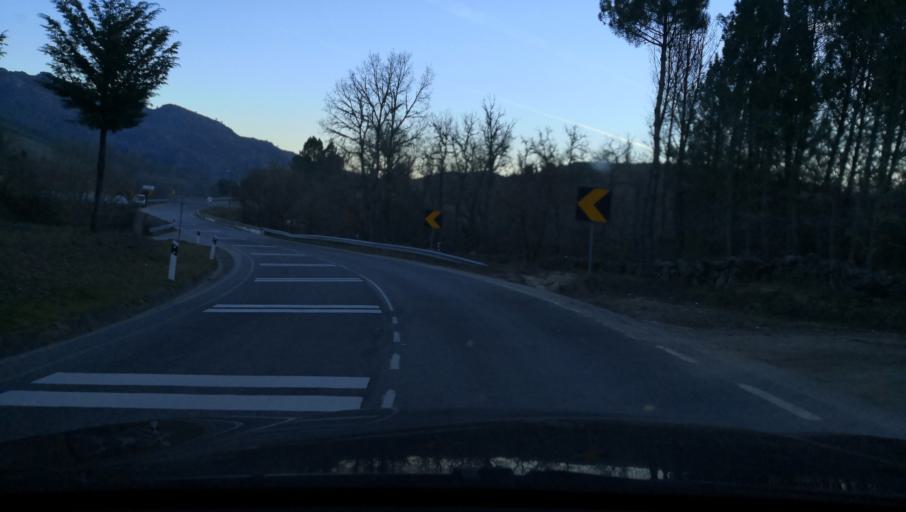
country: PT
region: Vila Real
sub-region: Vila Pouca de Aguiar
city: Vila Pouca de Aguiar
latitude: 41.4217
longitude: -7.6858
